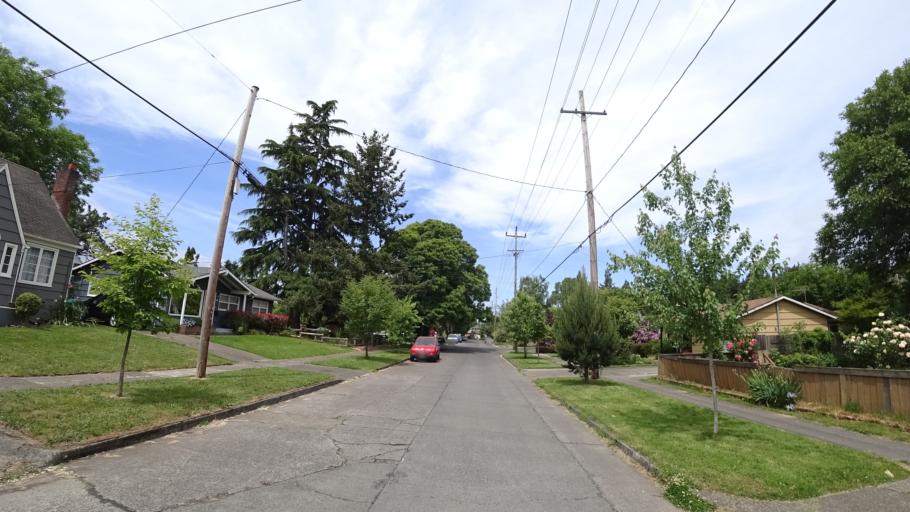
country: US
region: Oregon
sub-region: Washington County
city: West Haven
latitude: 45.5967
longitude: -122.7553
